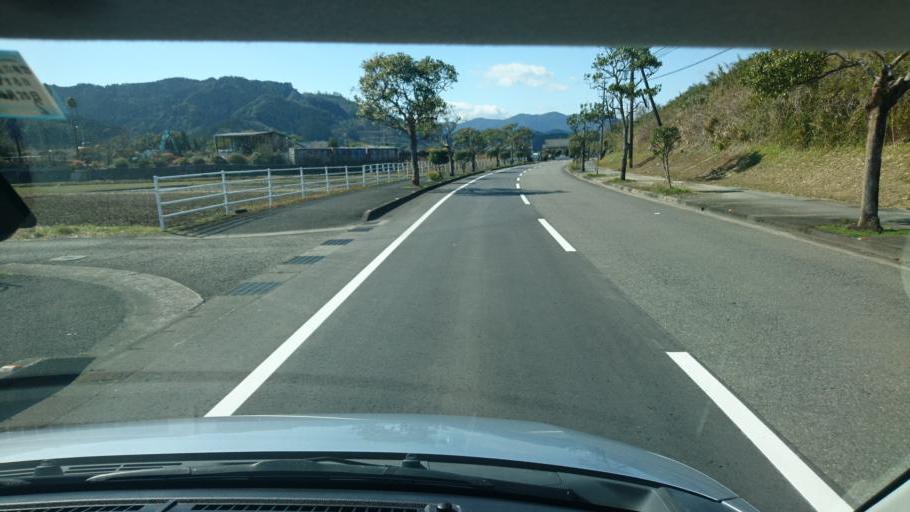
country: JP
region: Miyazaki
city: Miyazaki-shi
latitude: 31.8248
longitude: 131.4251
